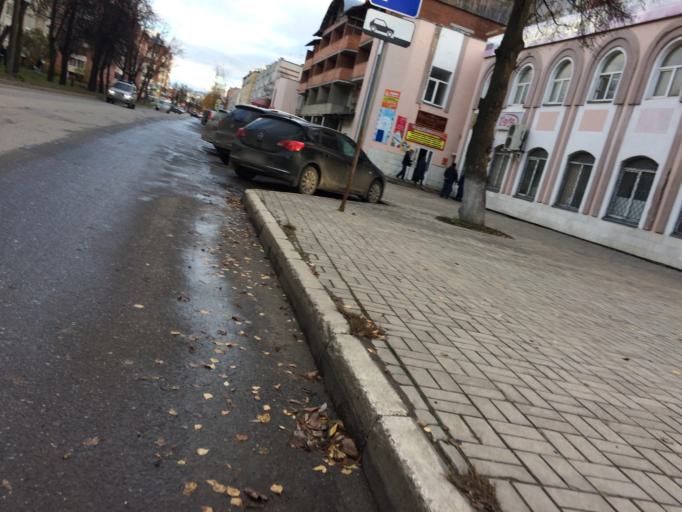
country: RU
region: Mariy-El
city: Yoshkar-Ola
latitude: 56.6443
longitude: 47.8991
